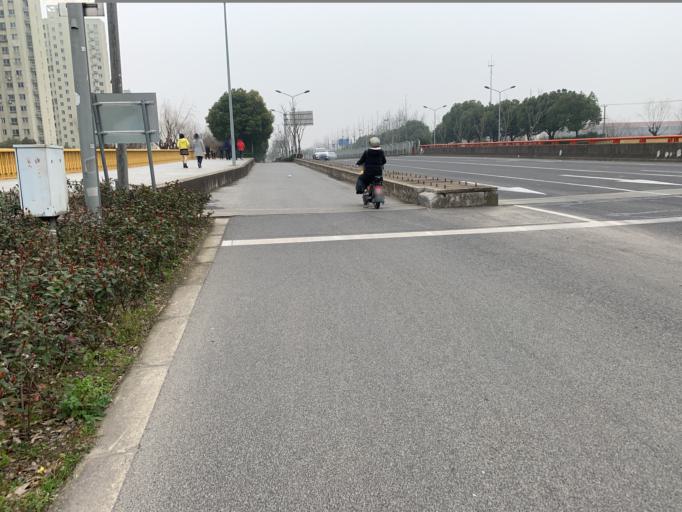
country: CN
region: Shanghai Shi
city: Huamu
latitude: 31.2440
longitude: 121.6213
